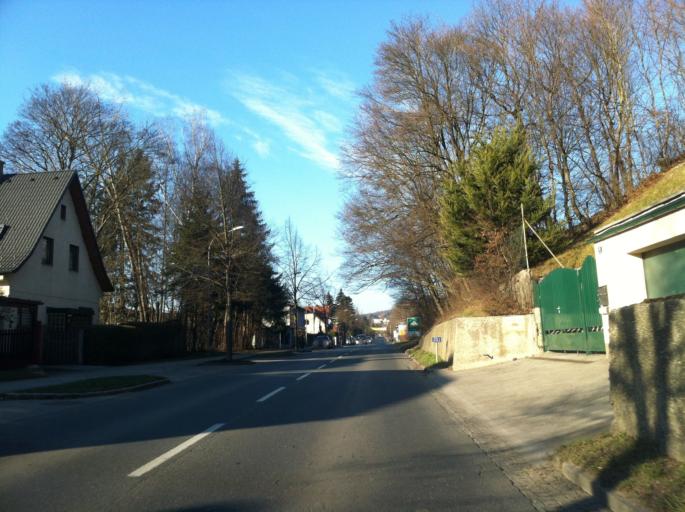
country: AT
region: Lower Austria
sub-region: Politischer Bezirk Wien-Umgebung
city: Gablitz
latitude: 48.2207
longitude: 16.1638
